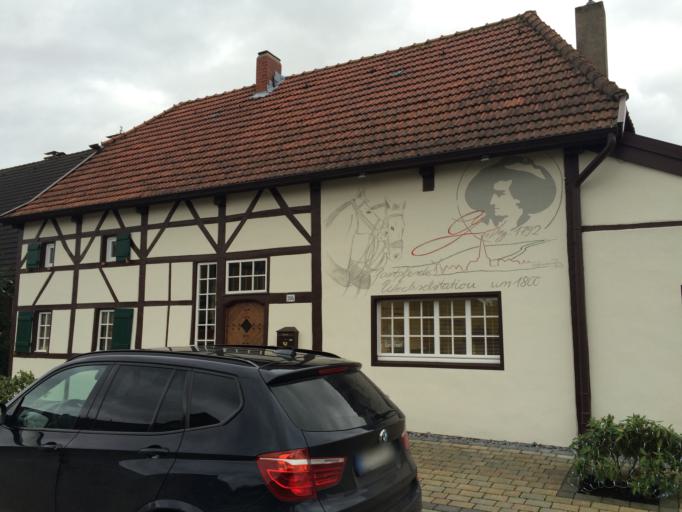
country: DE
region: North Rhine-Westphalia
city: Dorsten
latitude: 51.6781
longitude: 7.0143
